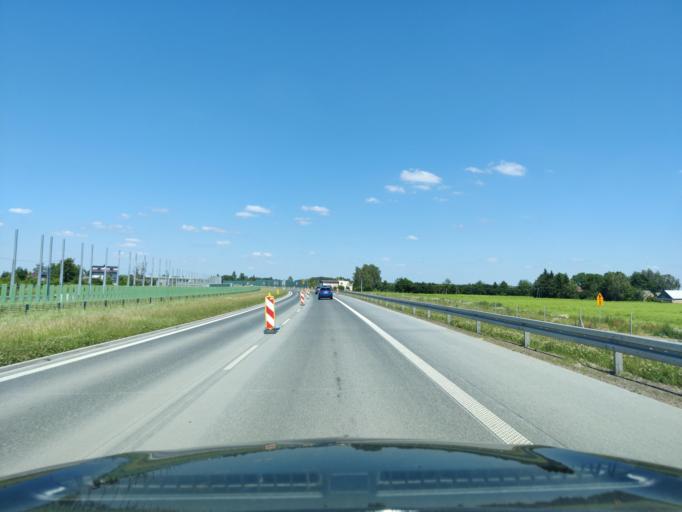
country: PL
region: Masovian Voivodeship
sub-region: Powiat plonski
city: Plonsk
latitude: 52.6509
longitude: 20.3779
